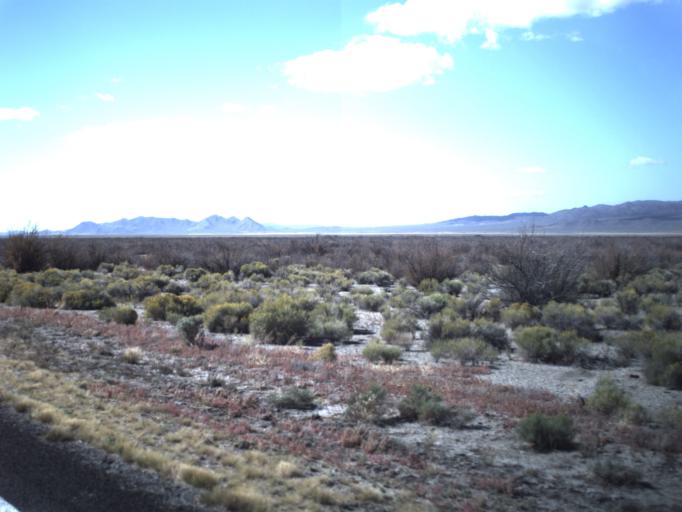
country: US
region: Utah
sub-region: Beaver County
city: Milford
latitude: 38.5708
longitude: -112.9900
